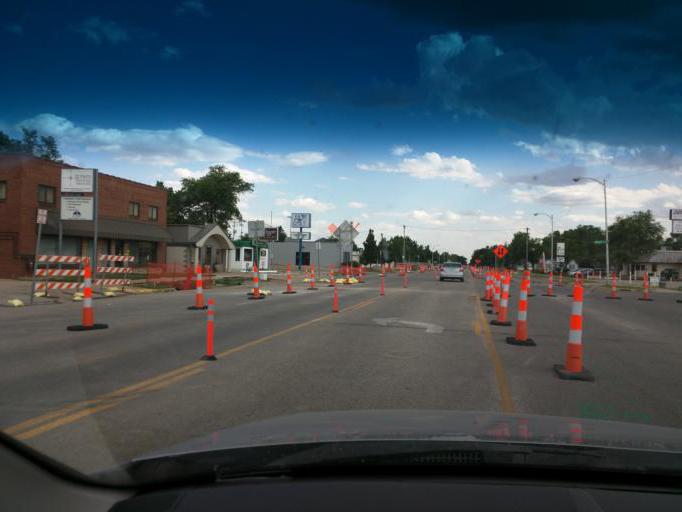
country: US
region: Kansas
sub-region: Reno County
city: Hutchinson
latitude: 38.0802
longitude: -97.9319
